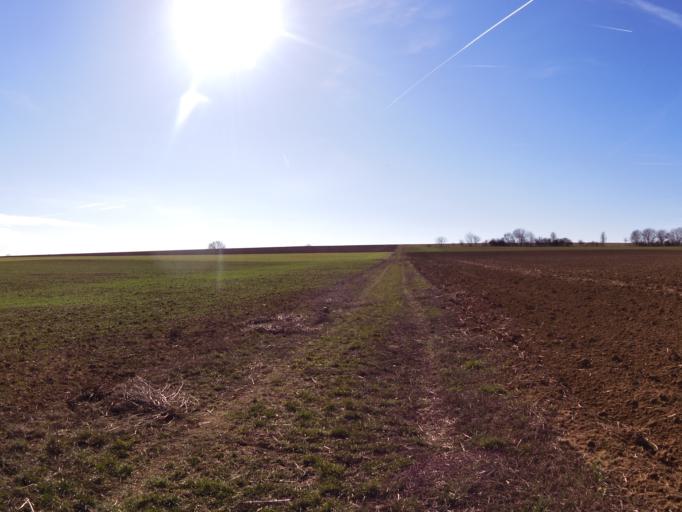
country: DE
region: Bavaria
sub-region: Regierungsbezirk Unterfranken
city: Kurnach
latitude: 49.8491
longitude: 10.0236
